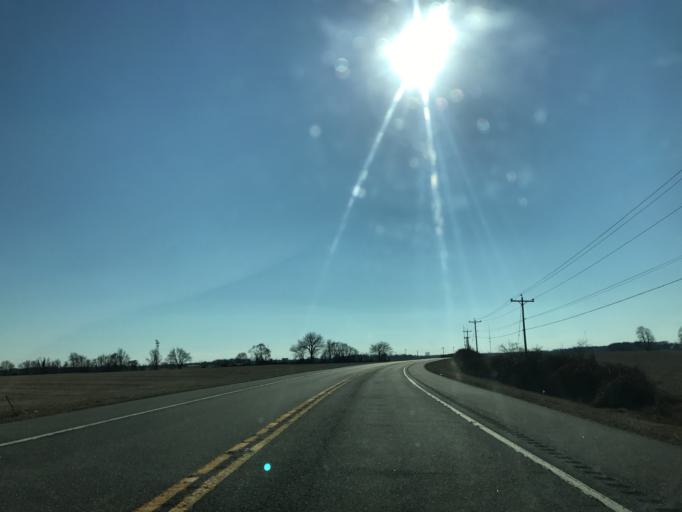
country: US
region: Maryland
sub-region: Queen Anne's County
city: Centreville
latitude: 38.9723
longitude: -76.0716
